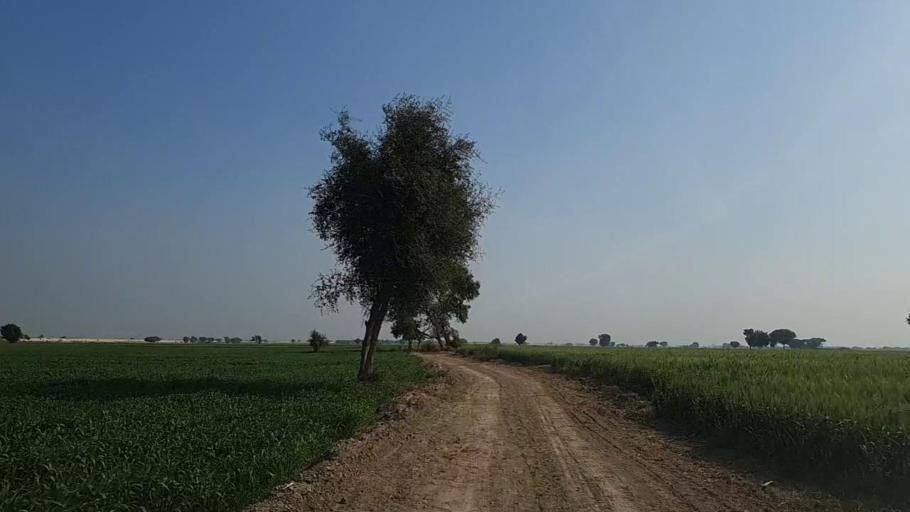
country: PK
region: Sindh
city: Moro
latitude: 26.6803
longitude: 67.9364
